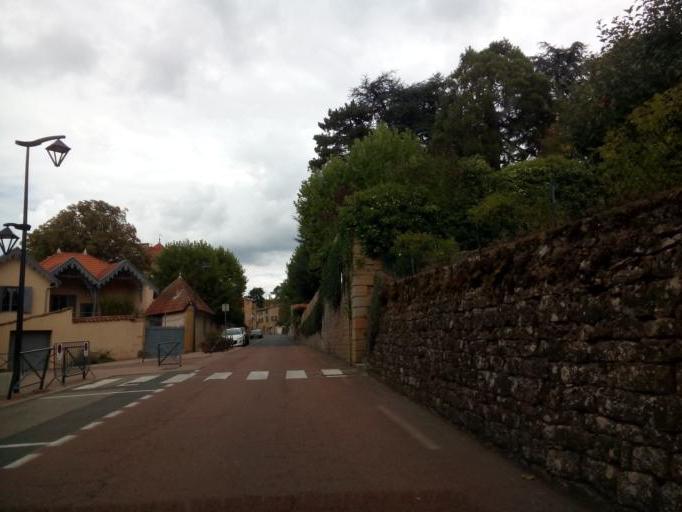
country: FR
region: Rhone-Alpes
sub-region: Departement du Rhone
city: Theize
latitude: 45.9189
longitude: 4.5820
